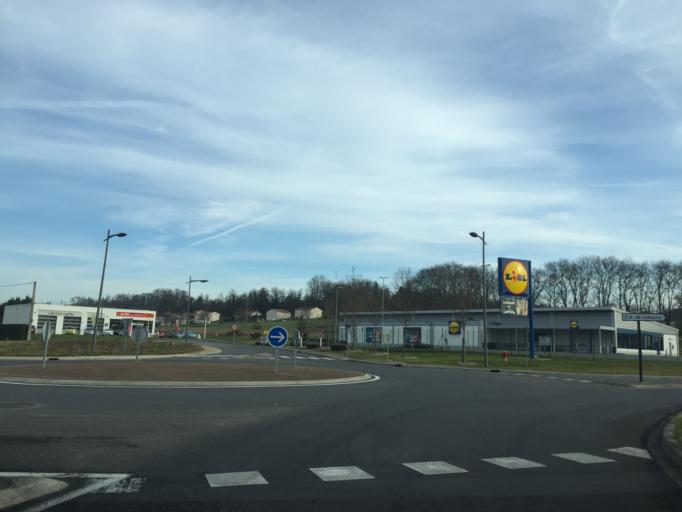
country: FR
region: Poitou-Charentes
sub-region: Departement de la Charente
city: Chalais
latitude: 45.2623
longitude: 0.0414
